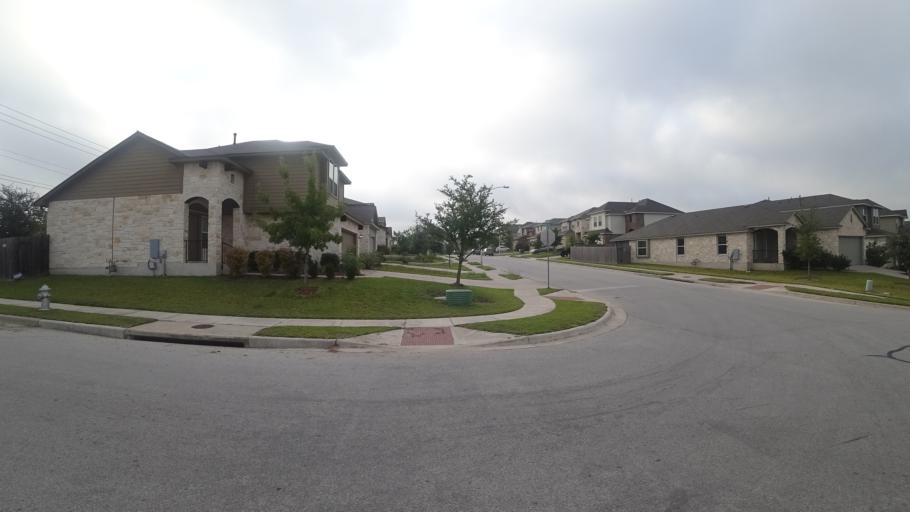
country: US
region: Texas
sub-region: Travis County
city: Pflugerville
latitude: 30.3683
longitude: -97.6526
